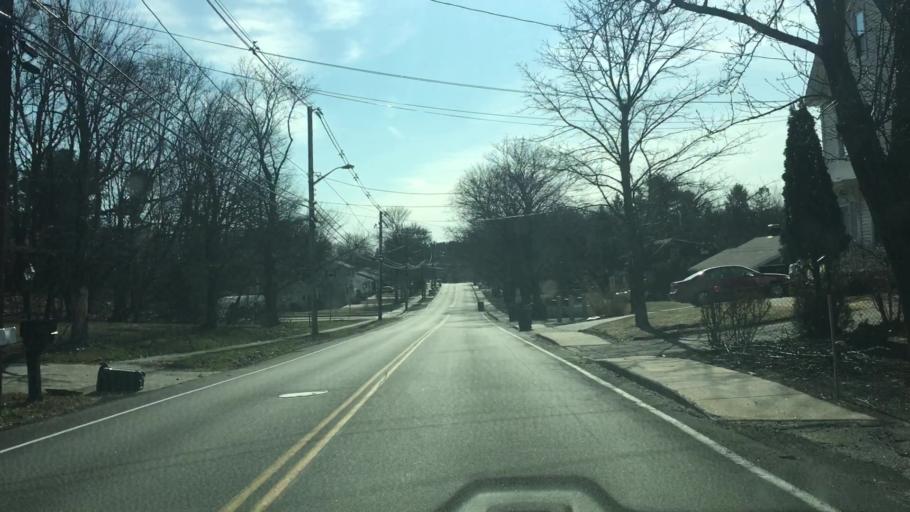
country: US
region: Massachusetts
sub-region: Essex County
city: Amesbury
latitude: 42.8552
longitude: -70.9506
